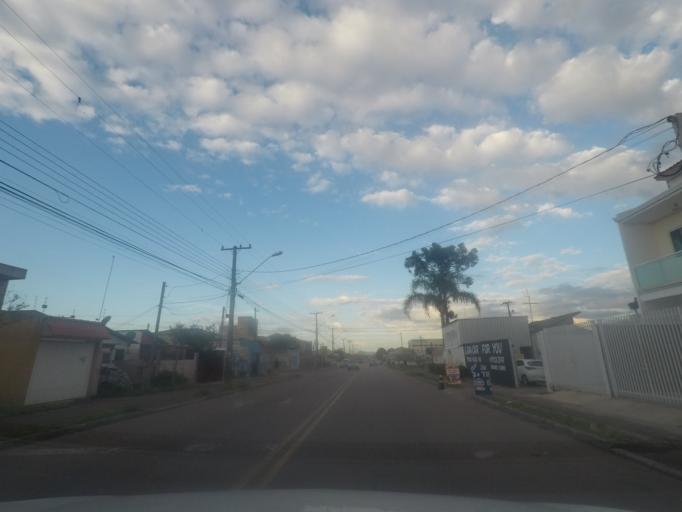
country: BR
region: Parana
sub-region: Pinhais
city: Pinhais
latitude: -25.4667
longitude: -49.2038
